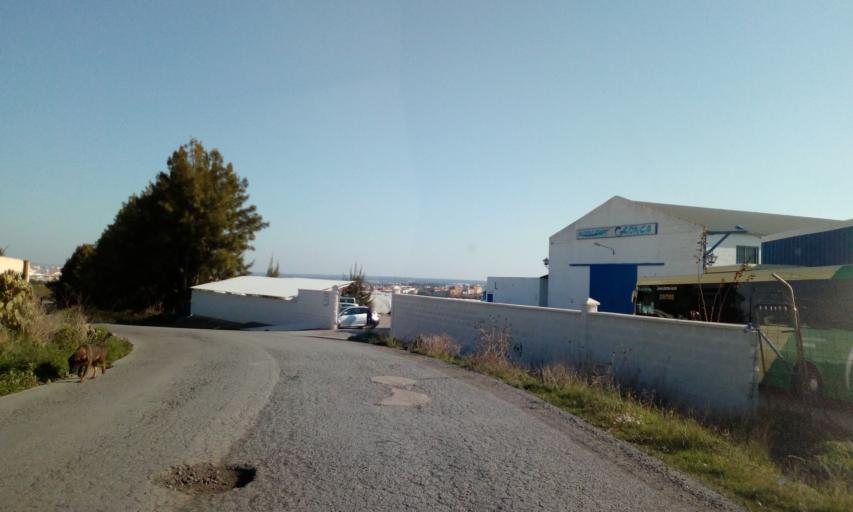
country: ES
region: Andalusia
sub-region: Provincia de Huelva
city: Lepe
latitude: 37.2470
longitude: -7.2168
